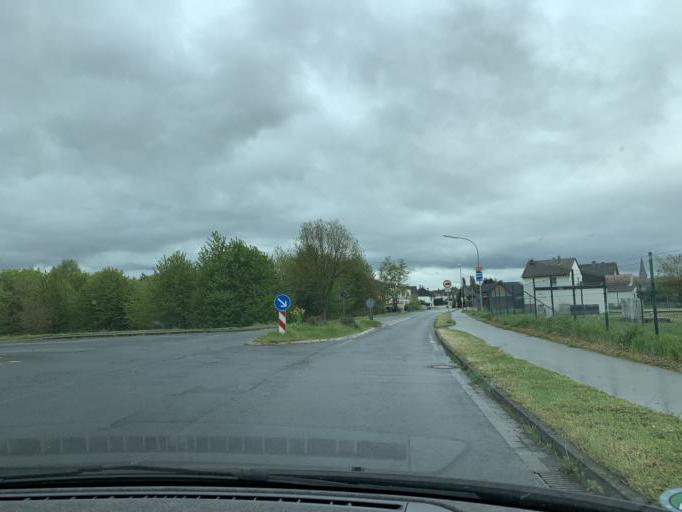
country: DE
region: North Rhine-Westphalia
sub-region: Regierungsbezirk Koln
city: Mechernich
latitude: 50.6399
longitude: 6.6989
